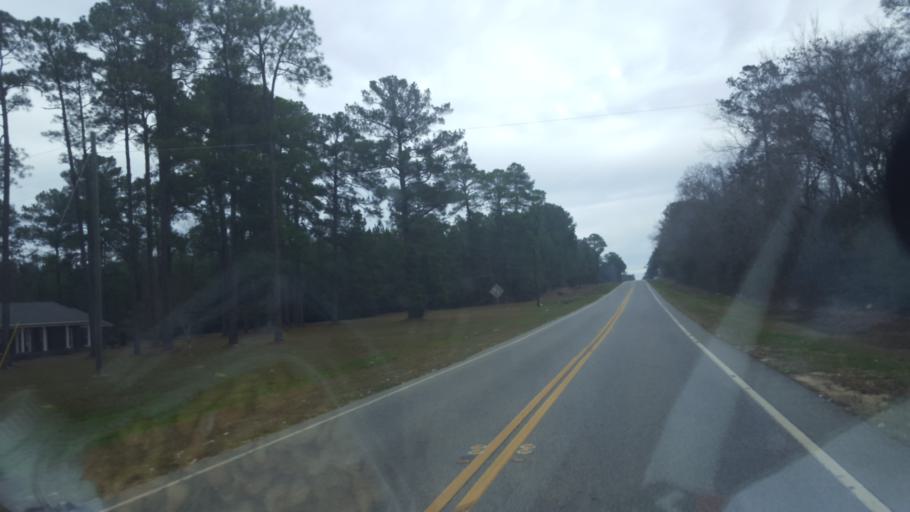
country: US
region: Georgia
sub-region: Wilcox County
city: Rochelle
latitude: 31.7965
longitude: -83.4972
